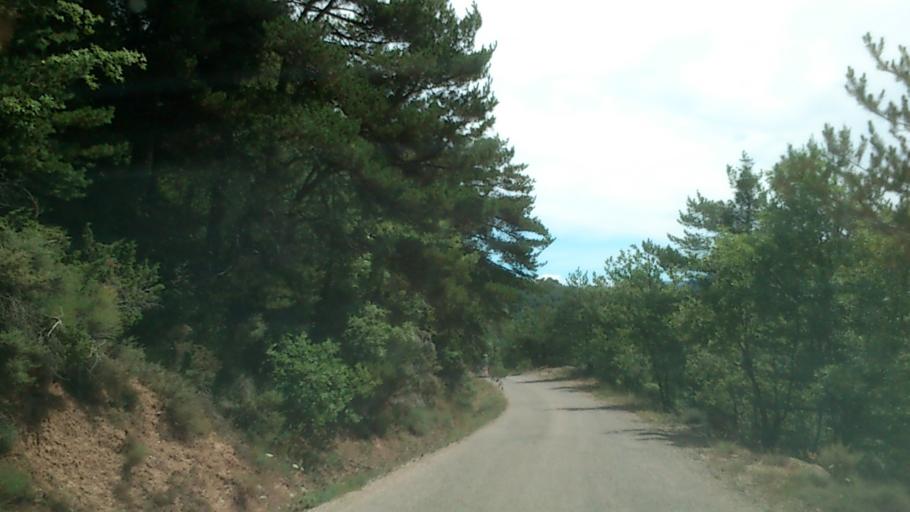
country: ES
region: Aragon
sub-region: Provincia de Huesca
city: Yebra de Basa
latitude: 42.3252
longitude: -0.2643
